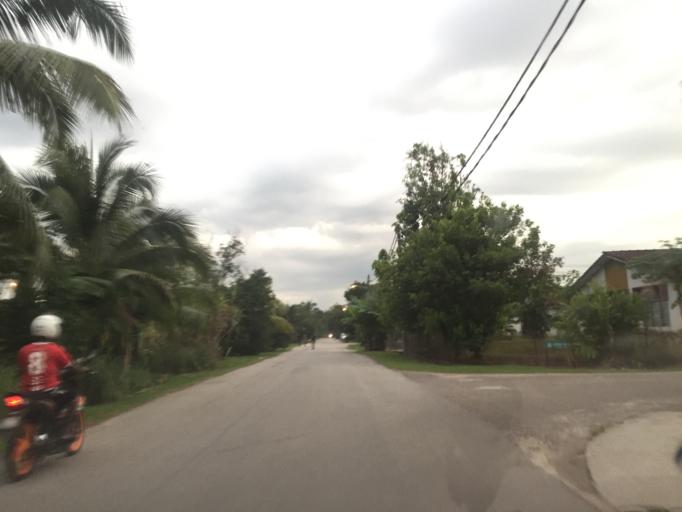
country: MY
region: Penang
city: Tasek Glugor
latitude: 5.5137
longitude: 100.5456
